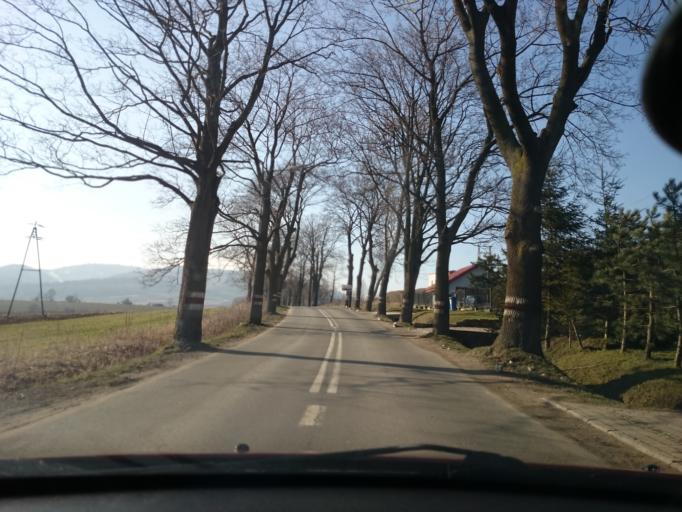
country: PL
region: Lower Silesian Voivodeship
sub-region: Powiat klodzki
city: Bystrzyca Klodzka
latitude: 50.3061
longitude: 16.6320
